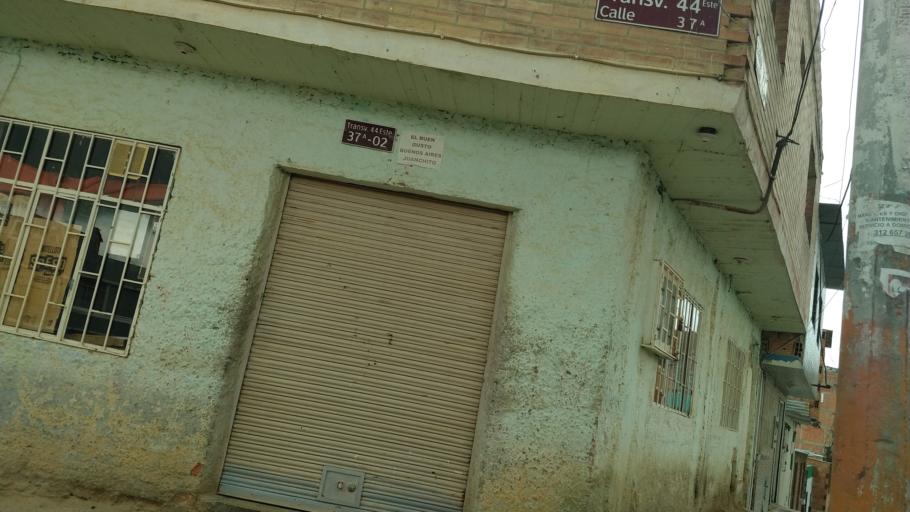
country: CO
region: Cundinamarca
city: Soacha
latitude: 4.5646
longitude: -74.1847
